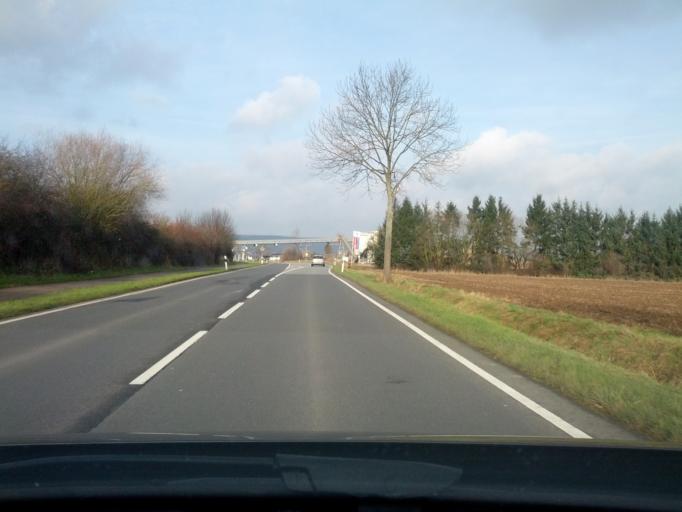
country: DE
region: North Rhine-Westphalia
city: Beverungen
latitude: 51.6478
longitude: 9.3923
